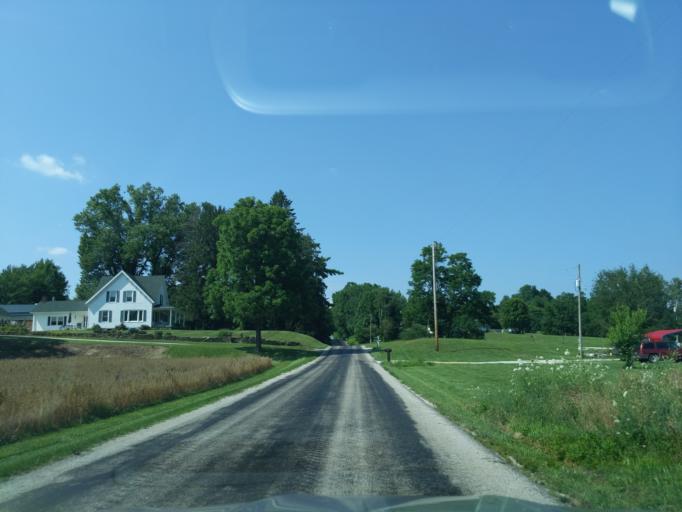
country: US
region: Indiana
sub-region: Ripley County
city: Osgood
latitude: 39.1125
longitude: -85.3435
